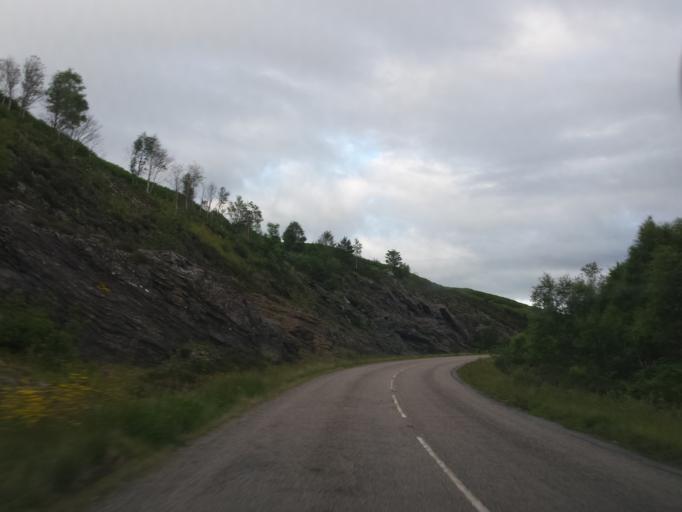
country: GB
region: Scotland
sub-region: Highland
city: Portree
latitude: 57.2889
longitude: -5.5806
